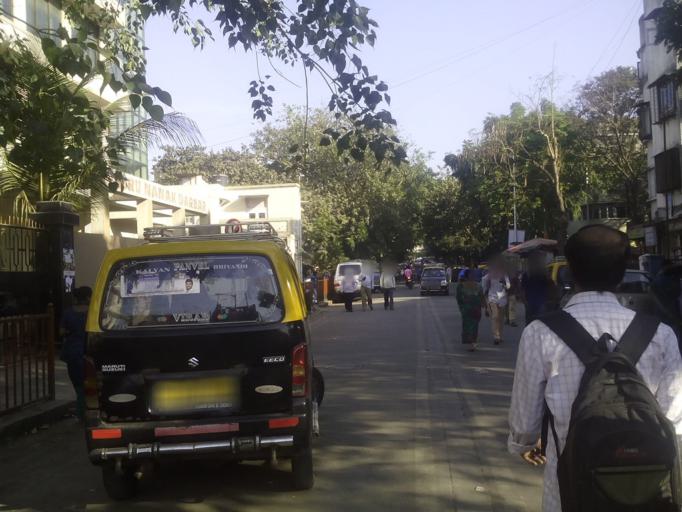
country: IN
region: Maharashtra
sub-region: Mumbai Suburban
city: Mumbai
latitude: 19.0403
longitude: 72.8598
